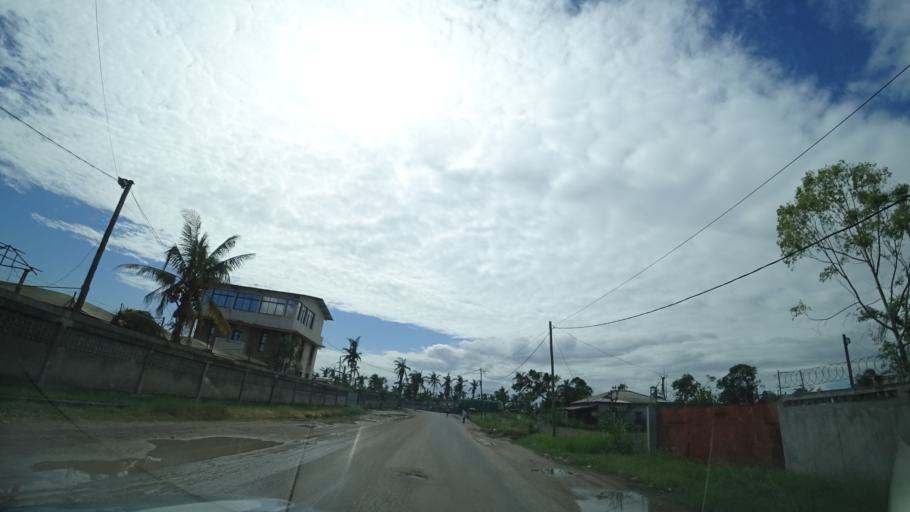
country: MZ
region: Sofala
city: Beira
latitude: -19.7563
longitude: 34.8636
